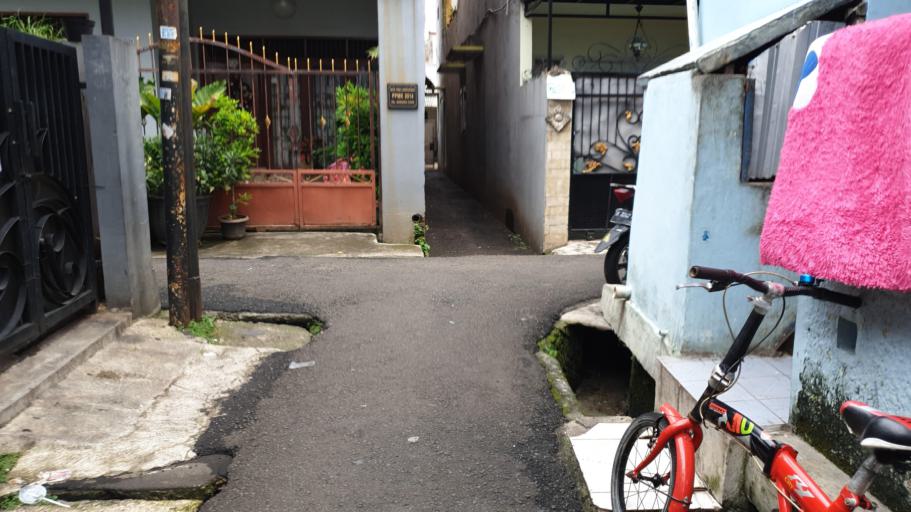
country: ID
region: Jakarta Raya
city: Jakarta
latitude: -6.2625
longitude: 106.7959
